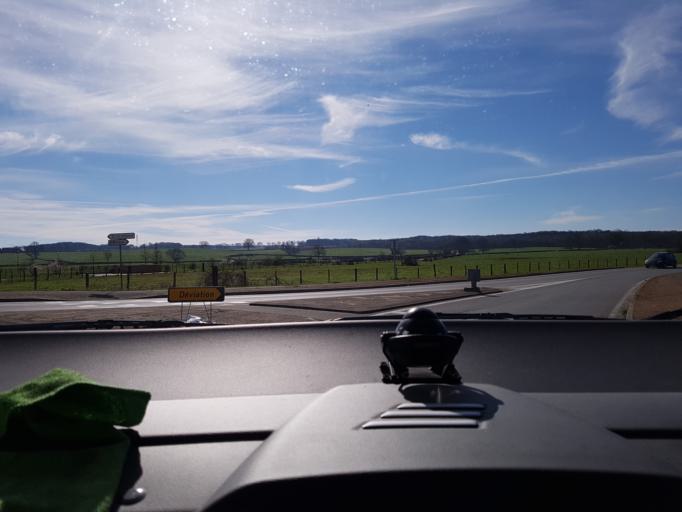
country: FR
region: Bourgogne
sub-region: Departement de Saone-et-Loire
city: Gueugnon
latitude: 46.5847
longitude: 4.0631
